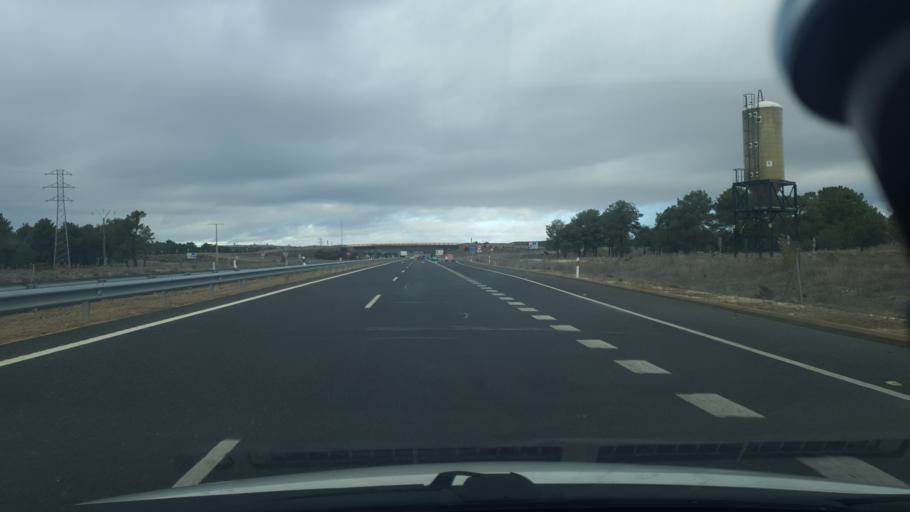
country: ES
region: Castille and Leon
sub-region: Provincia de Segovia
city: Cuellar
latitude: 41.3661
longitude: -4.2987
